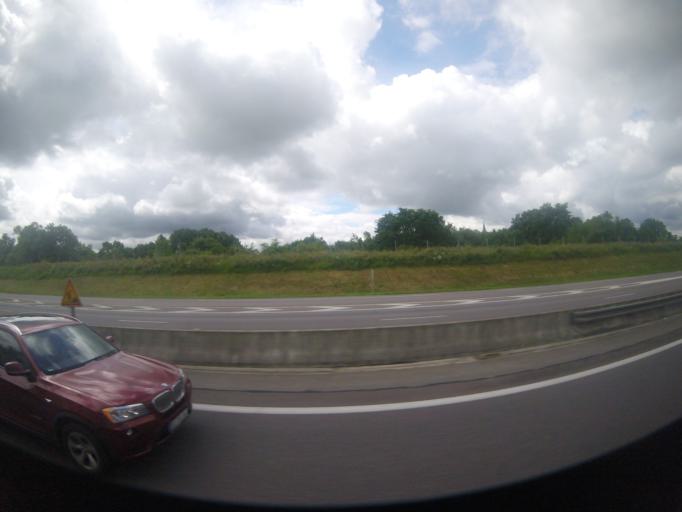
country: FR
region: Lorraine
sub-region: Departement de la Moselle
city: Argancy
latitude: 49.1985
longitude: 6.2050
